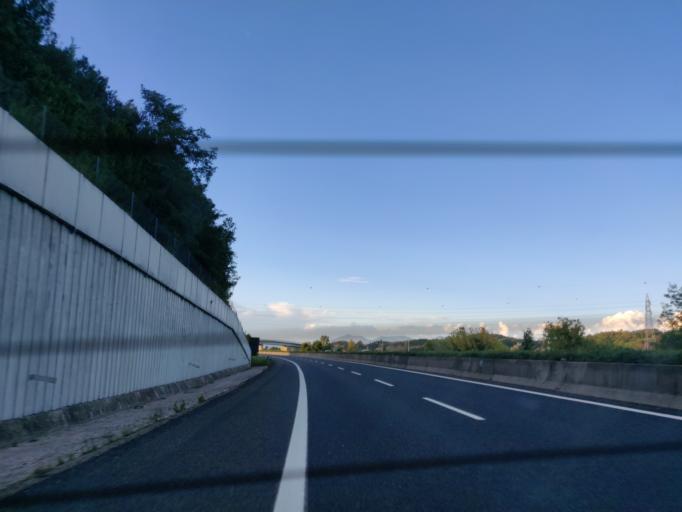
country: IT
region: Tuscany
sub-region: Provincia di Livorno
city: Collesalvetti
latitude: 43.5605
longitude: 10.4762
